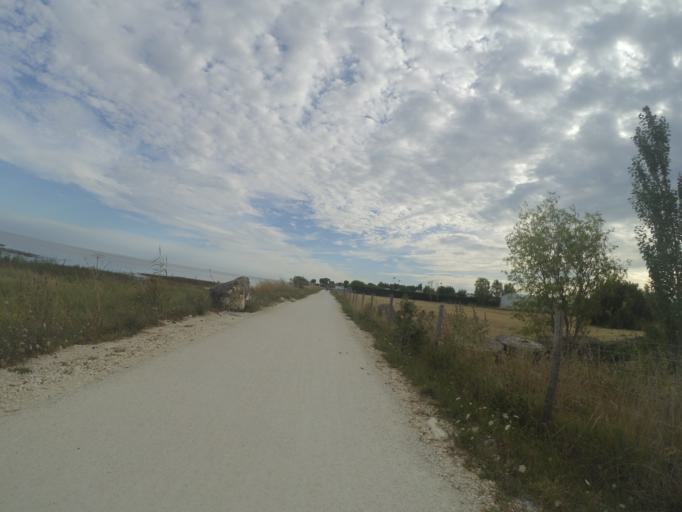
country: FR
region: Poitou-Charentes
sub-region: Departement de la Charente-Maritime
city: Meschers-sur-Gironde
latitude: 45.5569
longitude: -0.9422
